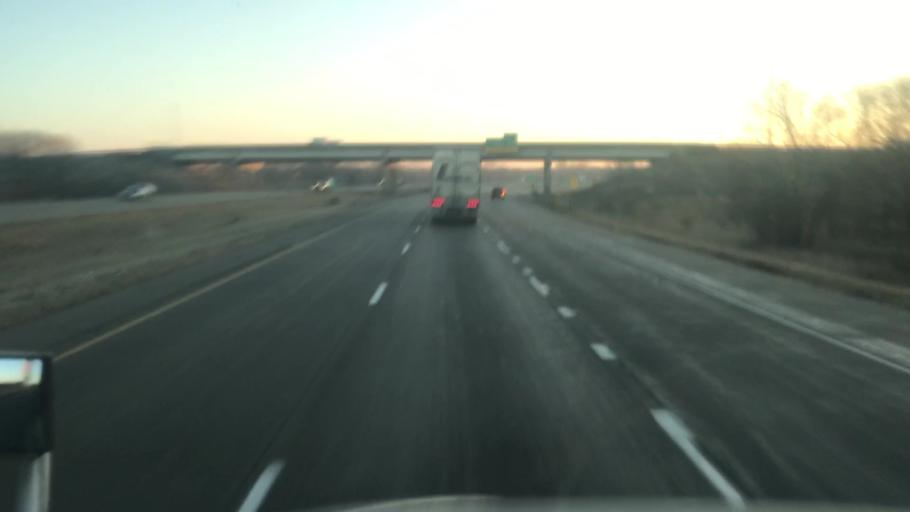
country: US
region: Iowa
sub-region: Black Hawk County
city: Evansdale
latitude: 42.4582
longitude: -92.2995
